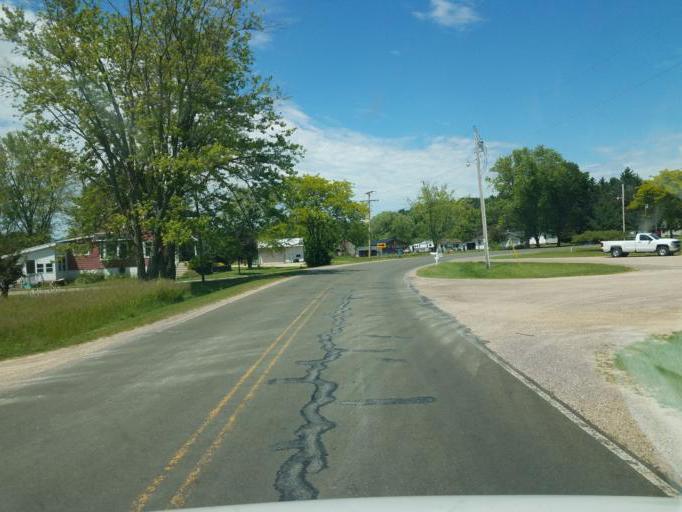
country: US
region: Wisconsin
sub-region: Juneau County
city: Elroy
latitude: 43.6455
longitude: -90.2219
